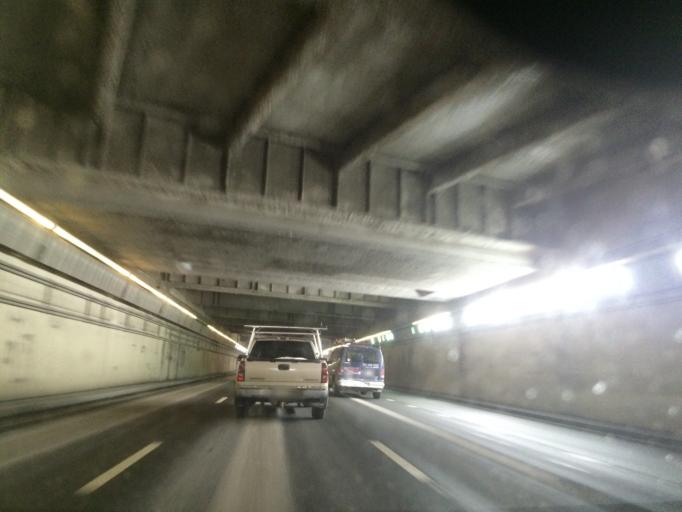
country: US
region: Massachusetts
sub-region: Suffolk County
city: Boston
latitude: 42.3476
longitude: -71.0848
